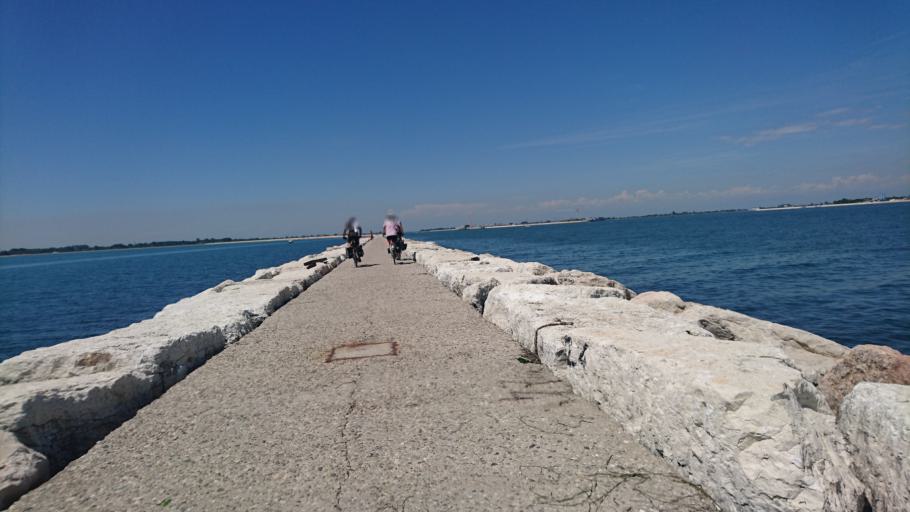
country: IT
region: Veneto
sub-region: Provincia di Venezia
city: Ca' Savio
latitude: 45.4204
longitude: 12.4235
